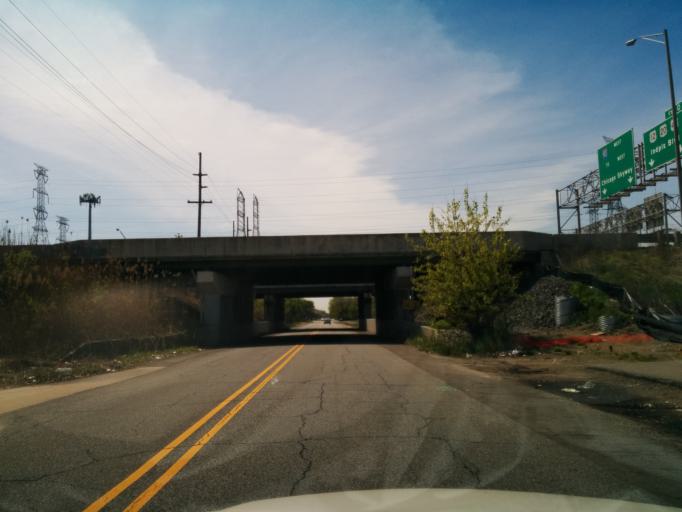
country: US
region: Indiana
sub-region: Lake County
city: Whiting
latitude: 41.6918
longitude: -87.5212
